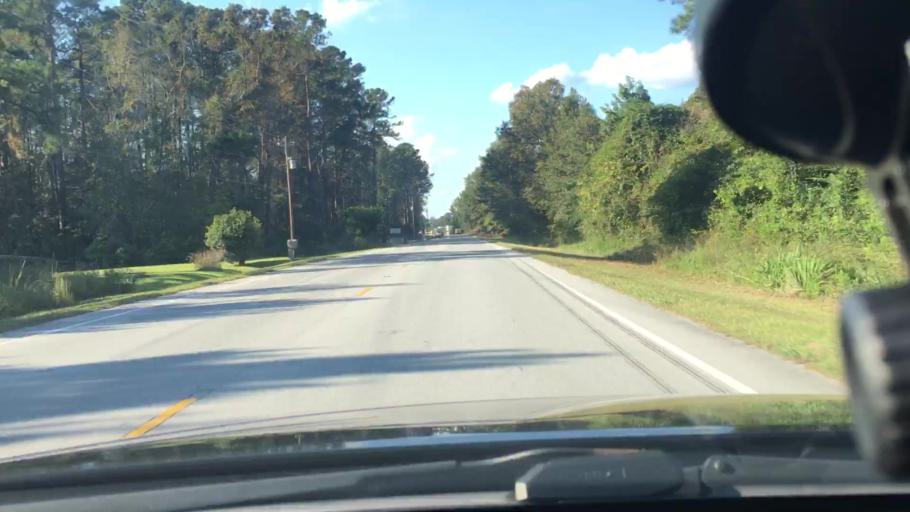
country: US
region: North Carolina
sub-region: Craven County
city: New Bern
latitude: 35.2138
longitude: -77.0628
